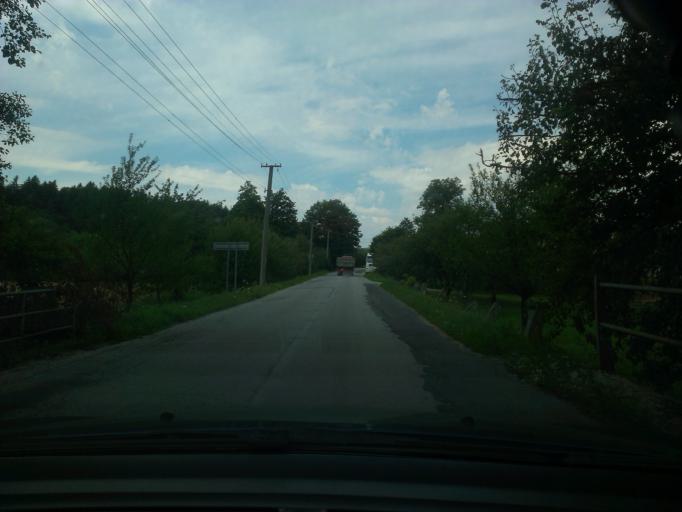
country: SK
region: Trenciansky
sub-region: Okres Myjava
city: Myjava
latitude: 48.7765
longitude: 17.5803
